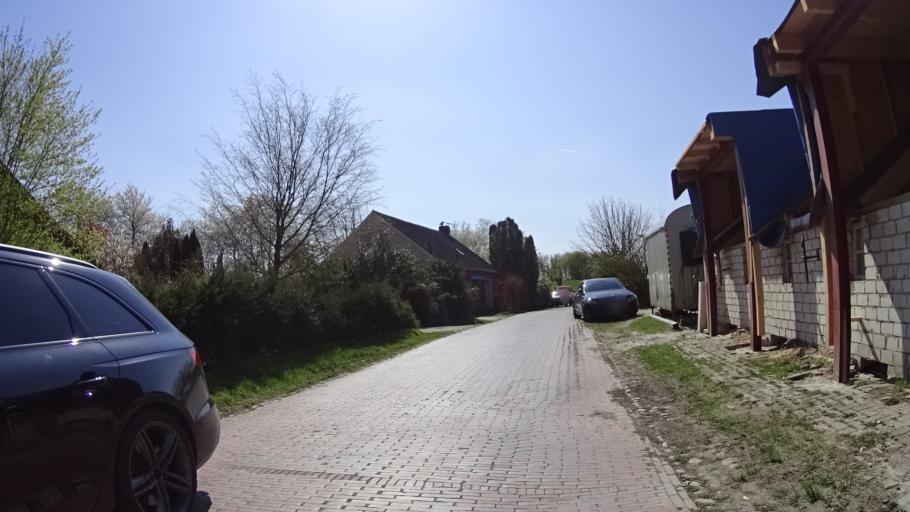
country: DE
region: Lower Saxony
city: Weener
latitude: 53.2000
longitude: 7.4040
